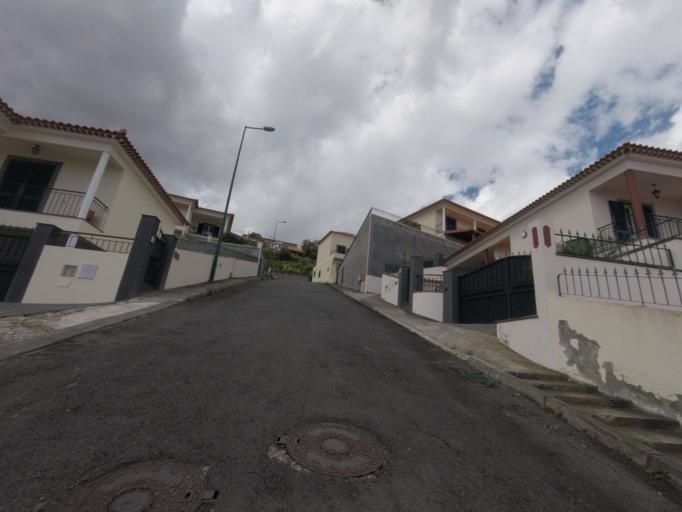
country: PT
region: Madeira
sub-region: Funchal
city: Nossa Senhora do Monte
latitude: 32.6678
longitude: -16.9093
